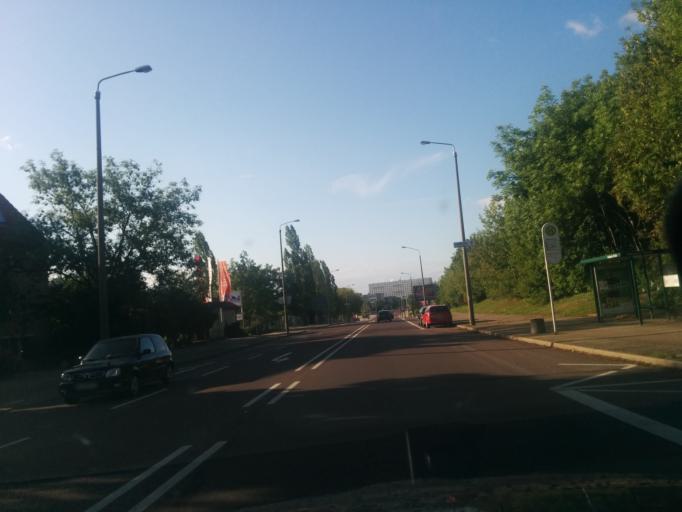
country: DE
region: Saxony-Anhalt
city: Halle Neustadt
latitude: 51.4853
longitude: 11.9092
